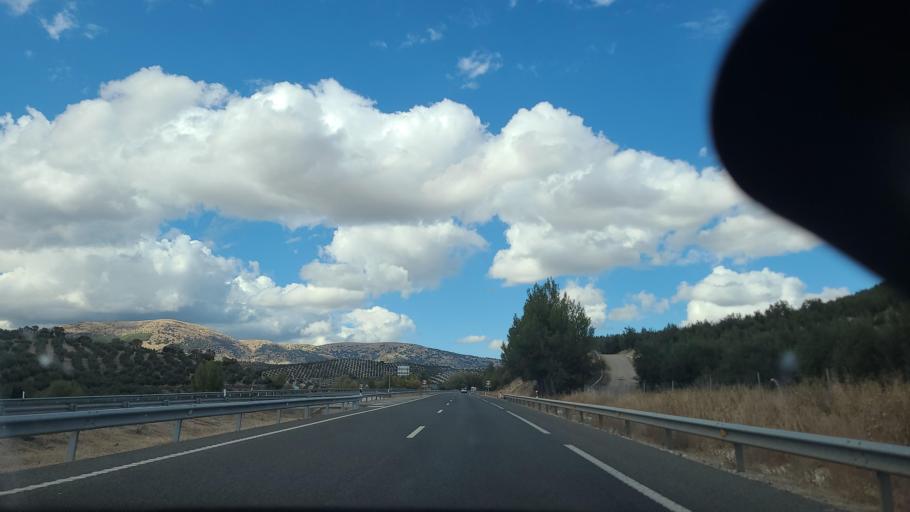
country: ES
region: Andalusia
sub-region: Provincia de Granada
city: Campotejar
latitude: 37.5090
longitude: -3.6333
